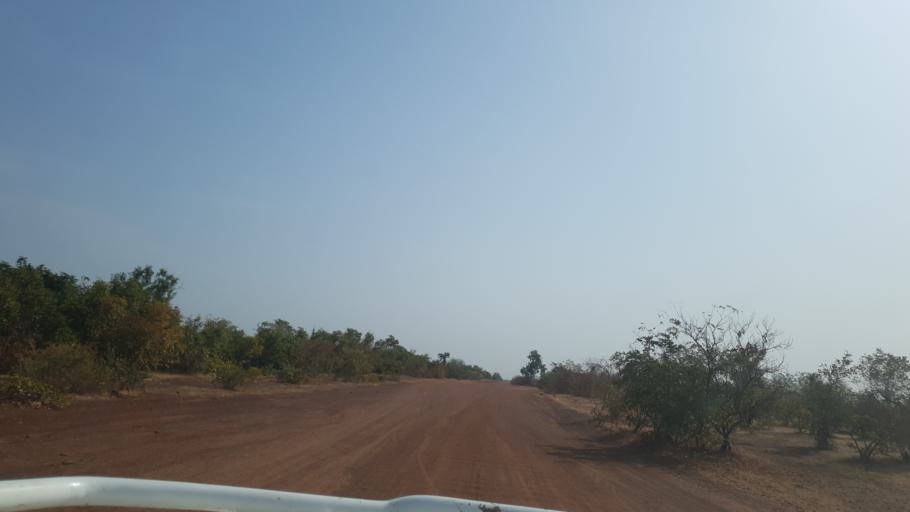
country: ML
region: Koulikoro
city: Dioila
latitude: 12.6675
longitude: -6.6976
